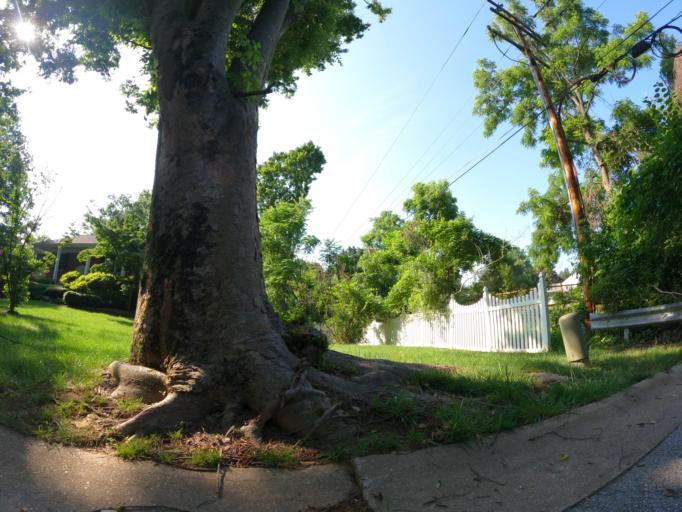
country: US
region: Maryland
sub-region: Howard County
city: Columbia
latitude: 39.2318
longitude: -76.8628
